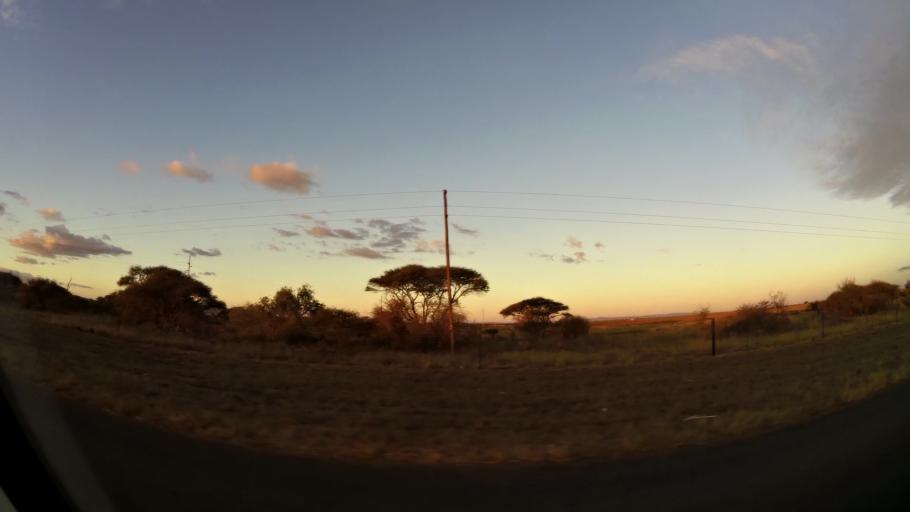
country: ZA
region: Limpopo
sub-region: Capricorn District Municipality
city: Polokwane
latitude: -23.7508
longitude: 29.4719
